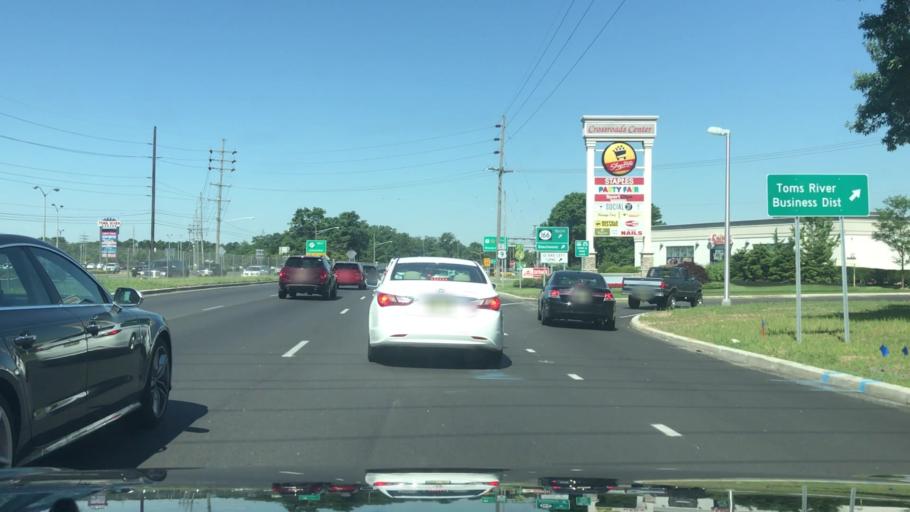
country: US
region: New Jersey
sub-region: Ocean County
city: Toms River
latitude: 39.9635
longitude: -74.2012
